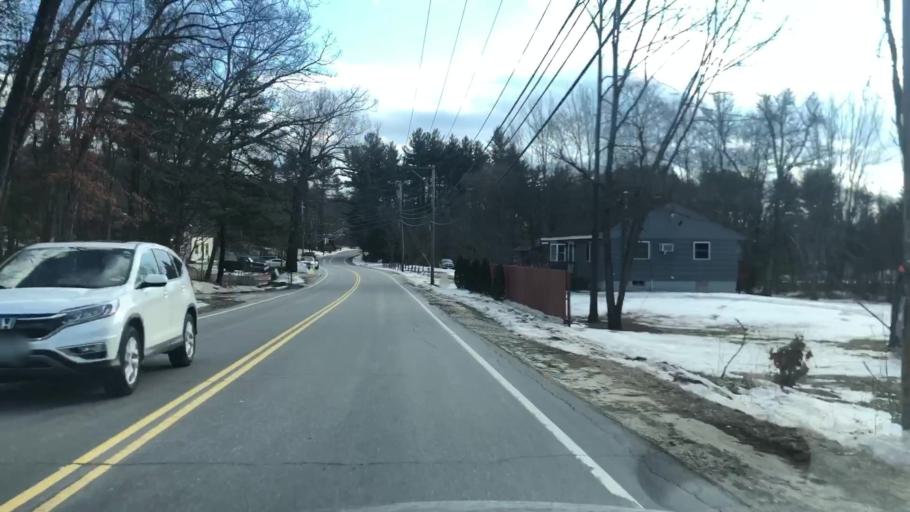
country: US
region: New Hampshire
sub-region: Hillsborough County
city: Milford
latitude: 42.8470
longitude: -71.6614
